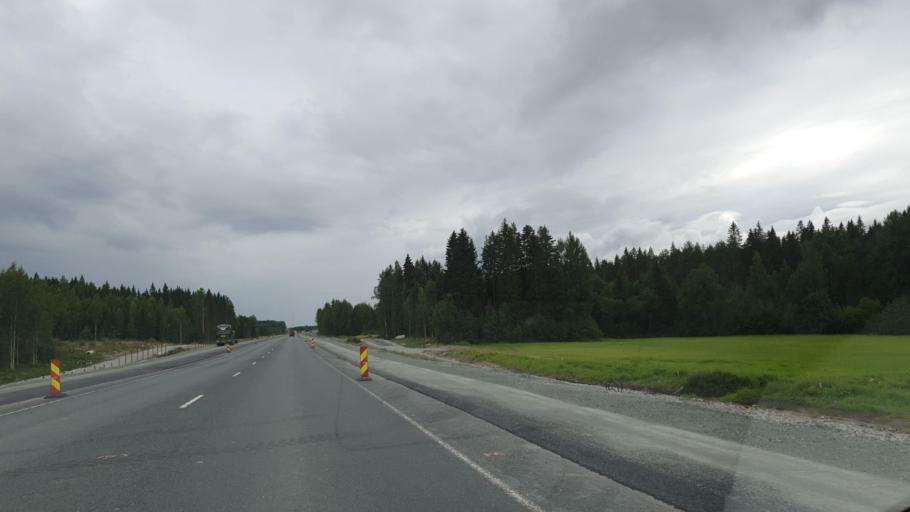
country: FI
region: Northern Savo
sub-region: Ylae-Savo
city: Lapinlahti
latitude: 63.2984
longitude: 27.4522
